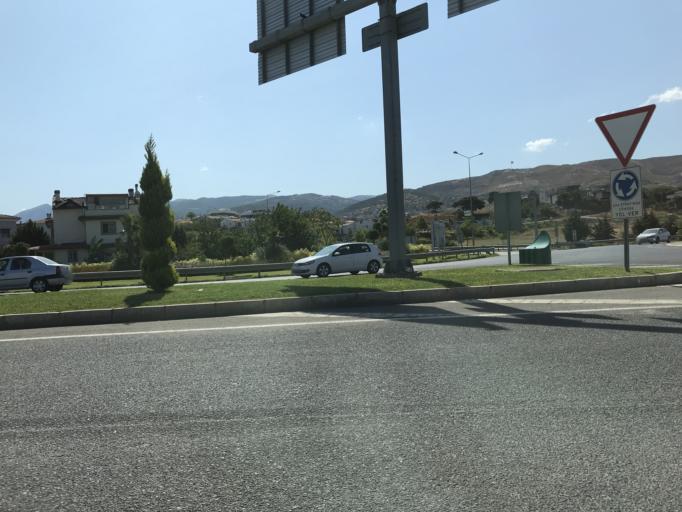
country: TR
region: Izmir
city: Urla
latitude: 38.3652
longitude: 26.8731
